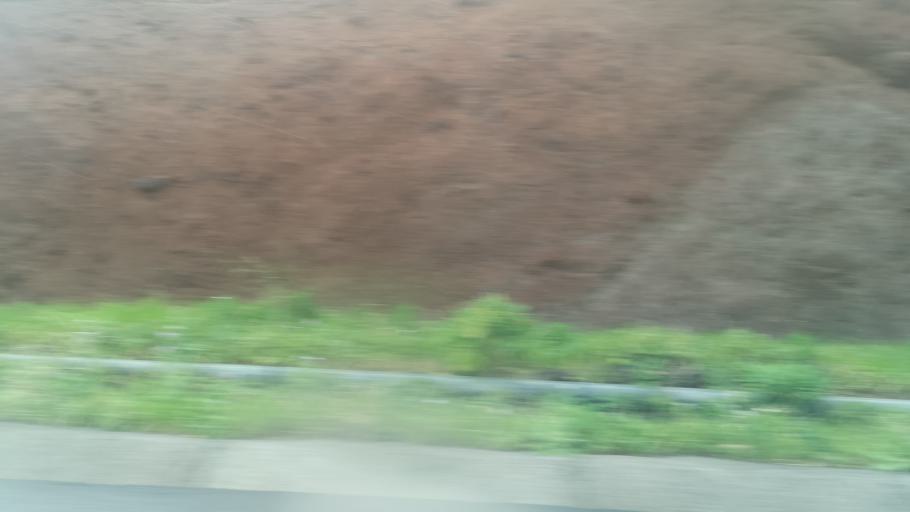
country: ES
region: Canary Islands
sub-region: Provincia de Santa Cruz de Tenerife
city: San Sebastian de la Gomera
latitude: 28.1198
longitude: -17.1439
